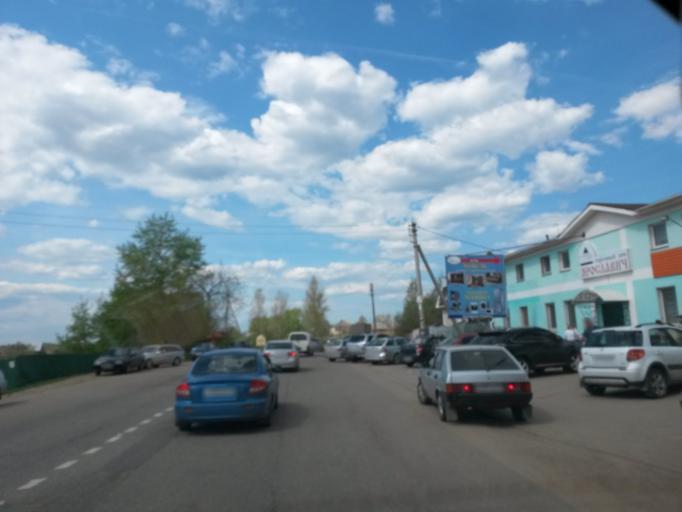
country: RU
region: Jaroslavl
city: Bol'shoye Selo
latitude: 57.7216
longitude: 38.9402
